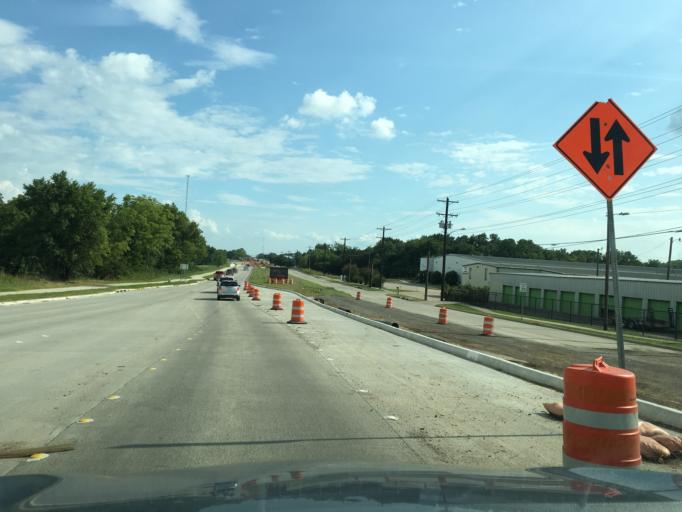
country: US
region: Texas
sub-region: Denton County
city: Denton
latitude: 33.2100
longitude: -97.0836
